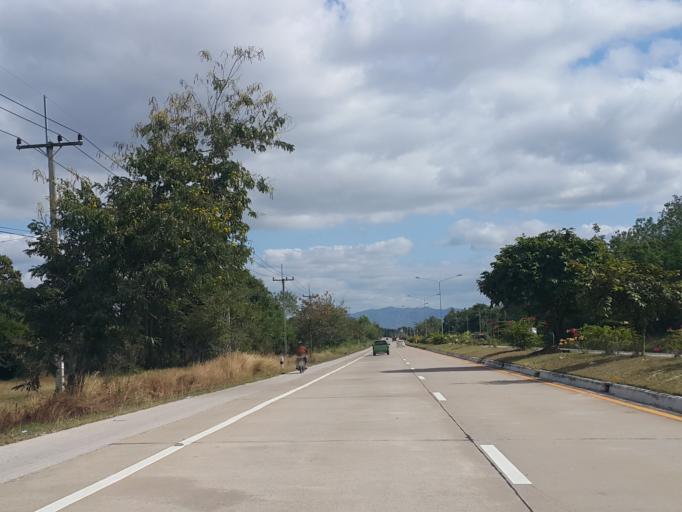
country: TH
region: Lampang
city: Hang Chat
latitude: 18.3241
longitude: 99.4195
